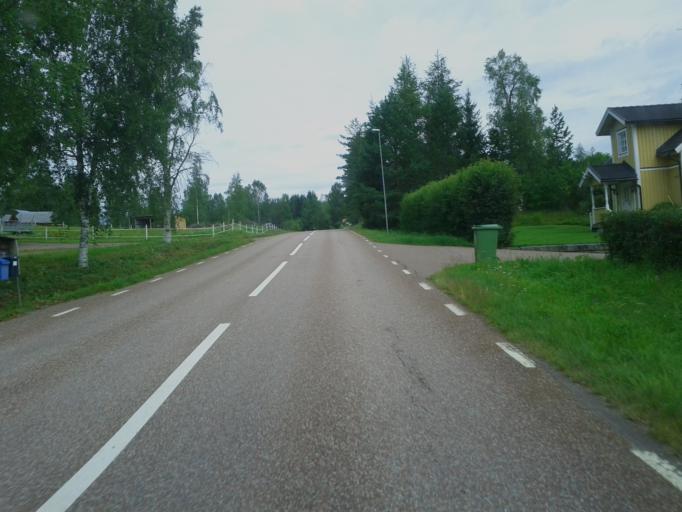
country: SE
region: Dalarna
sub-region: Borlange Kommun
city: Borlaenge
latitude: 60.3382
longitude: 15.4023
